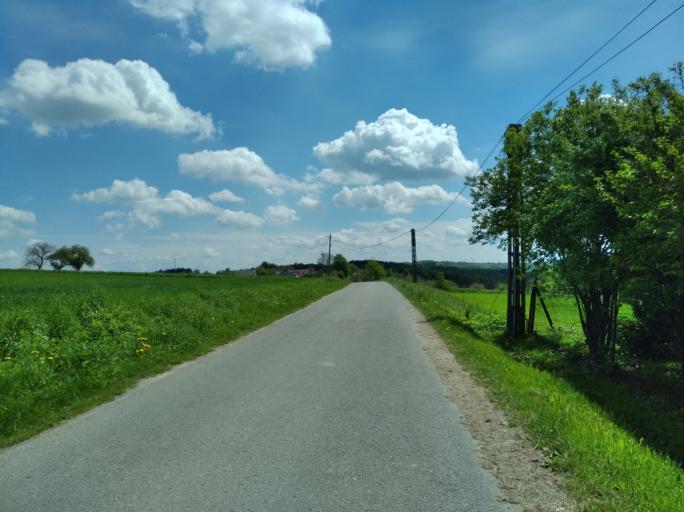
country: PL
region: Subcarpathian Voivodeship
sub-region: Powiat jasielski
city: Kolaczyce
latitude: 49.8420
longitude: 21.4573
